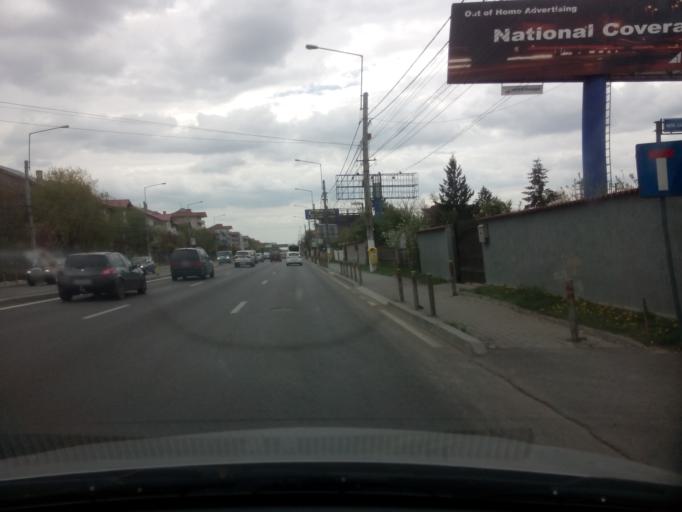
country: RO
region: Ilfov
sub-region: Comuna Otopeni
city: Otopeni
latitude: 44.5538
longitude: 26.0690
